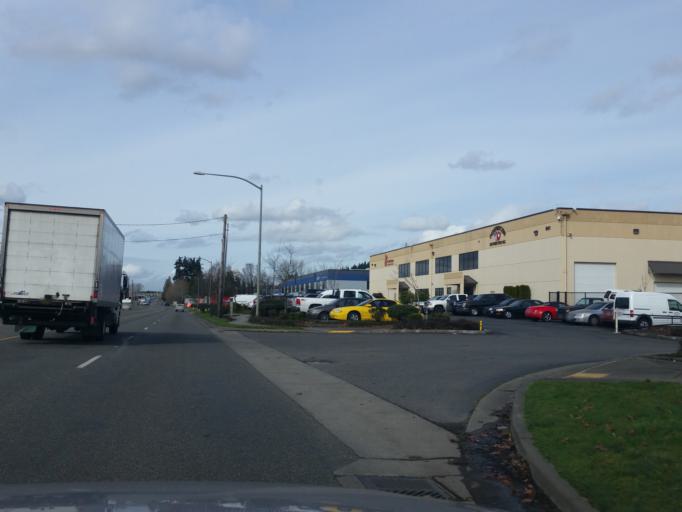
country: US
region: Washington
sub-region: Pierce County
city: North Puyallup
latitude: 47.2116
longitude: -122.3050
